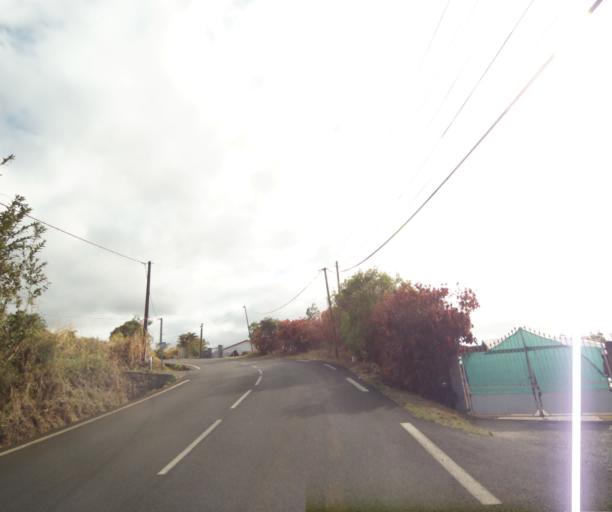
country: RE
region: Reunion
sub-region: Reunion
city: Saint-Paul
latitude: -21.0144
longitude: 55.3190
